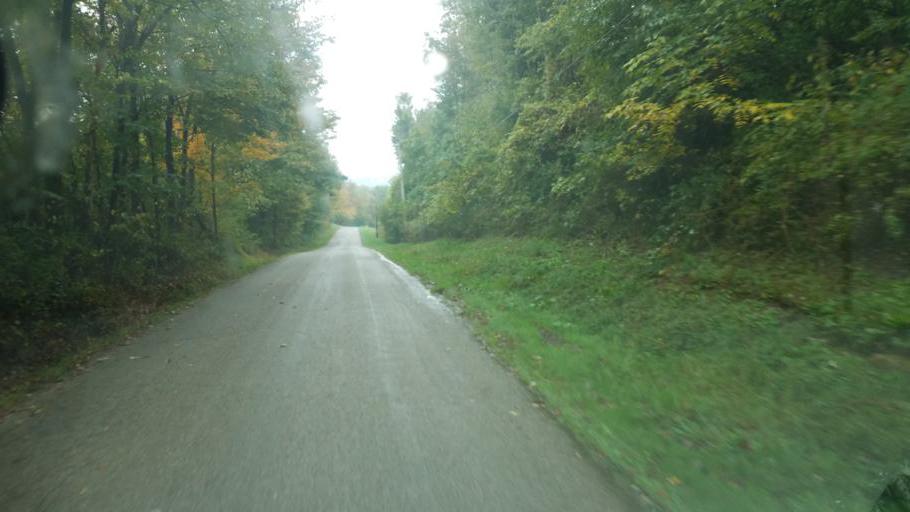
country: US
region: Ohio
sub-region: Sandusky County
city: Bellville
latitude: 40.5677
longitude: -82.4763
